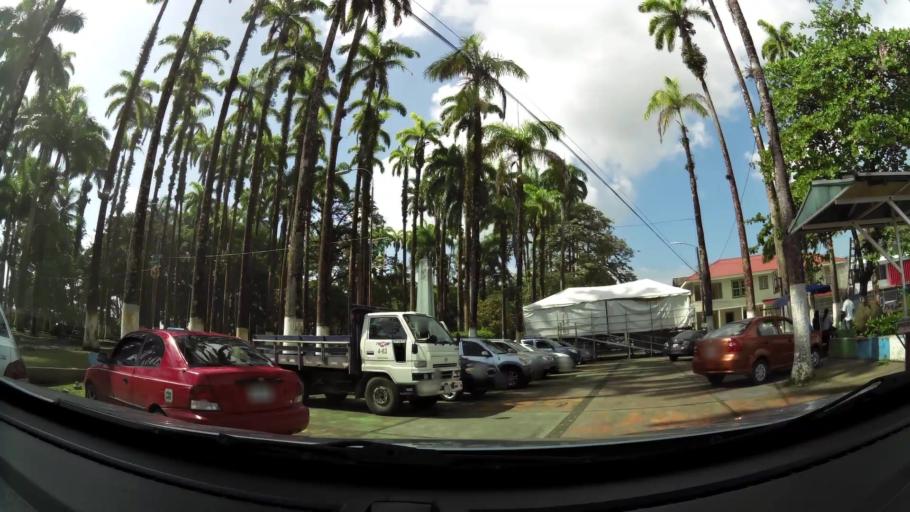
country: CR
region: Limon
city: Limon
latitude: 9.9933
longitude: -83.0248
